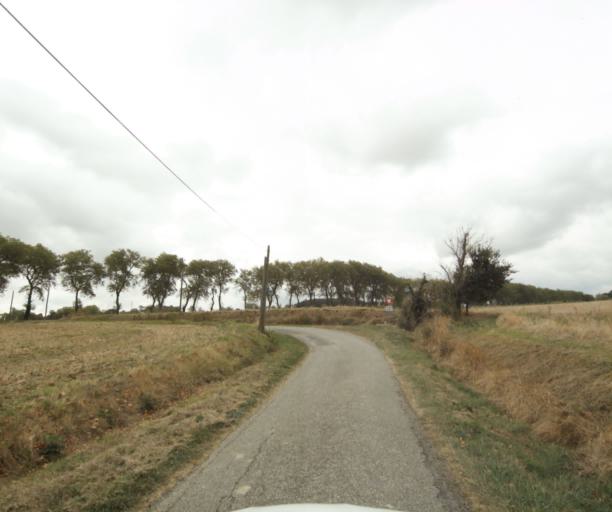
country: FR
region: Midi-Pyrenees
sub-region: Departement de la Haute-Garonne
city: Villefranche-de-Lauragais
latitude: 43.4151
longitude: 1.7386
